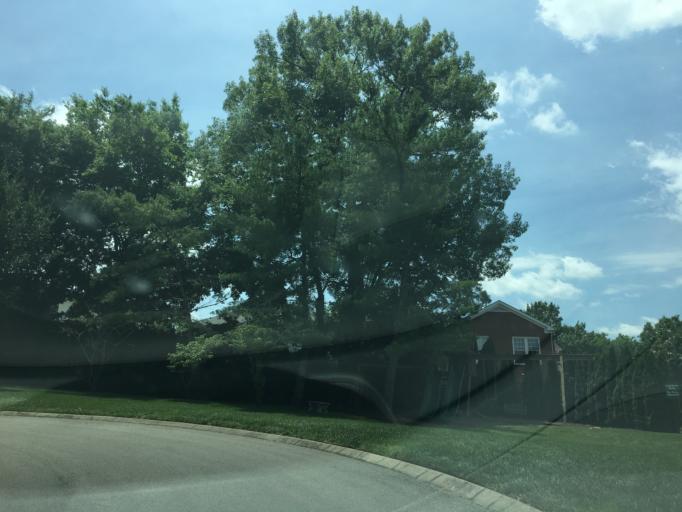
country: US
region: Tennessee
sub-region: Davidson County
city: Belle Meade
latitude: 36.1039
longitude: -86.8273
